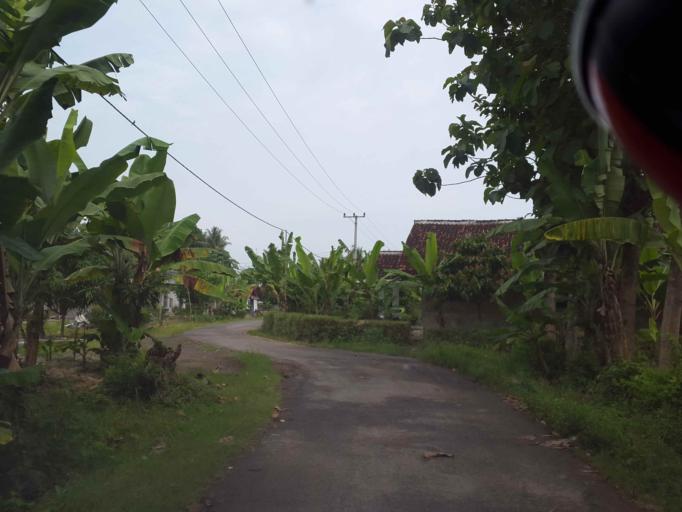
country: ID
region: Lampung
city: Natar
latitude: -5.2626
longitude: 105.2131
